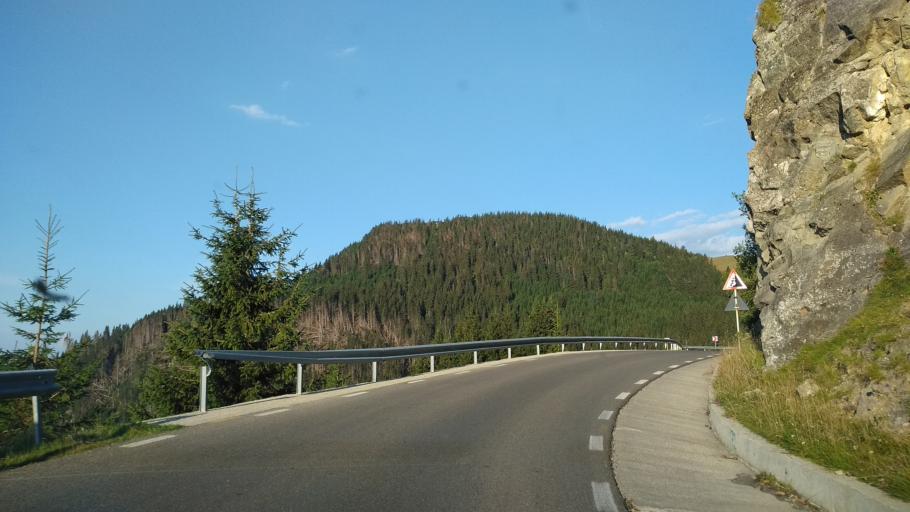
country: RO
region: Prahova
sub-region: Oras Sinaia
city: Sinaia
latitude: 45.3218
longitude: 25.4737
